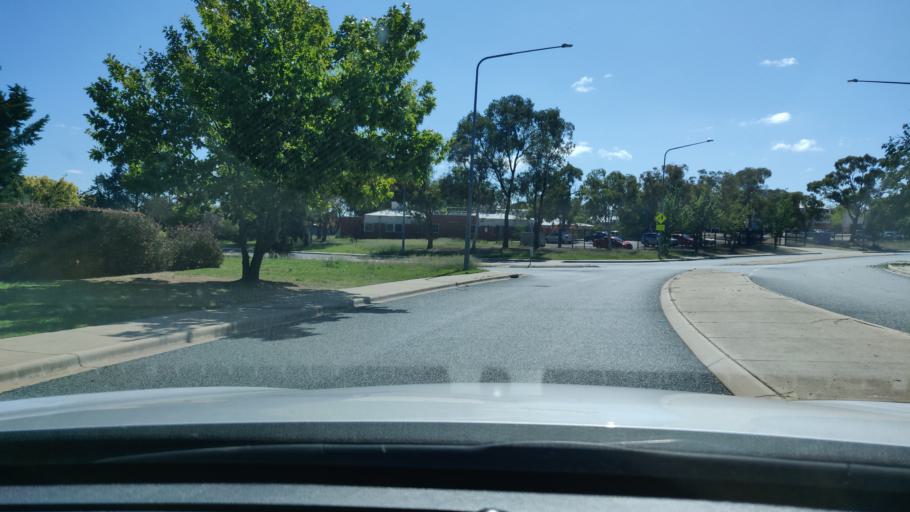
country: AU
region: Australian Capital Territory
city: Macarthur
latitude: -35.4296
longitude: 149.0883
